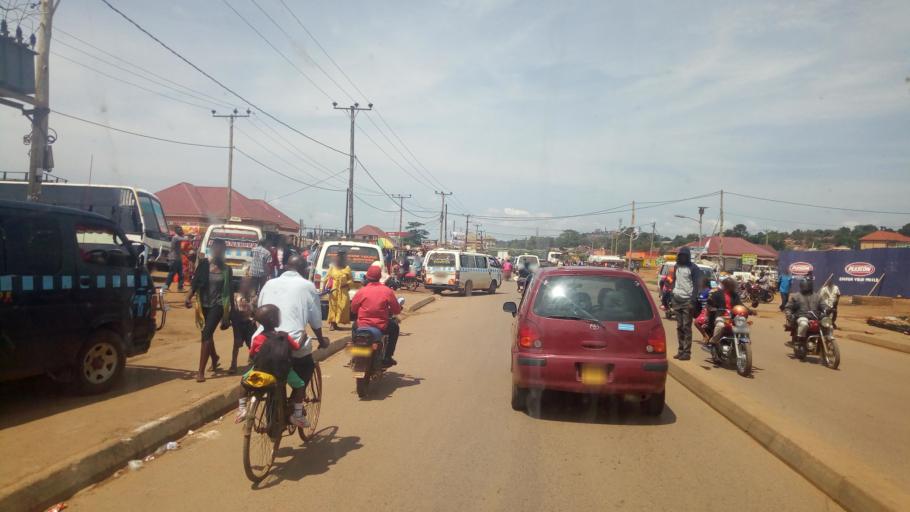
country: UG
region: Central Region
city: Kampala Central Division
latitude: 0.3538
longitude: 32.5723
